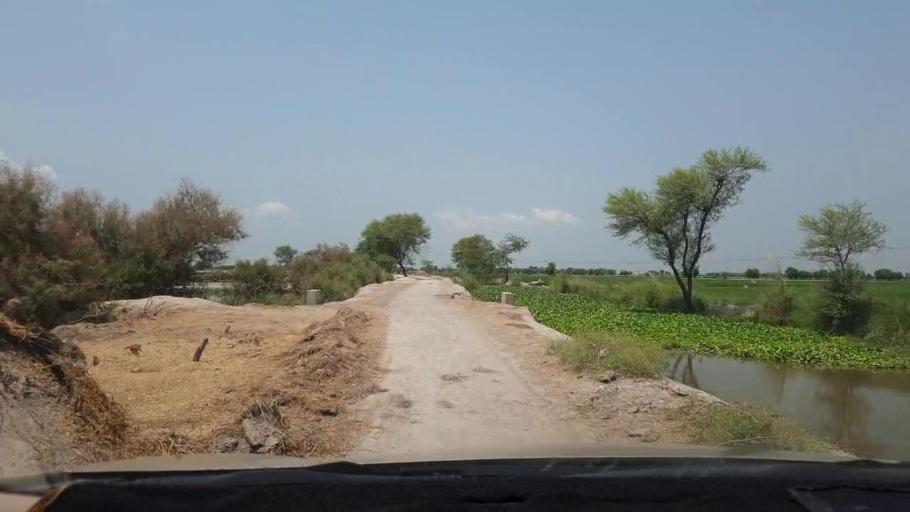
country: PK
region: Sindh
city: Naudero
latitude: 27.6717
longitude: 68.2977
